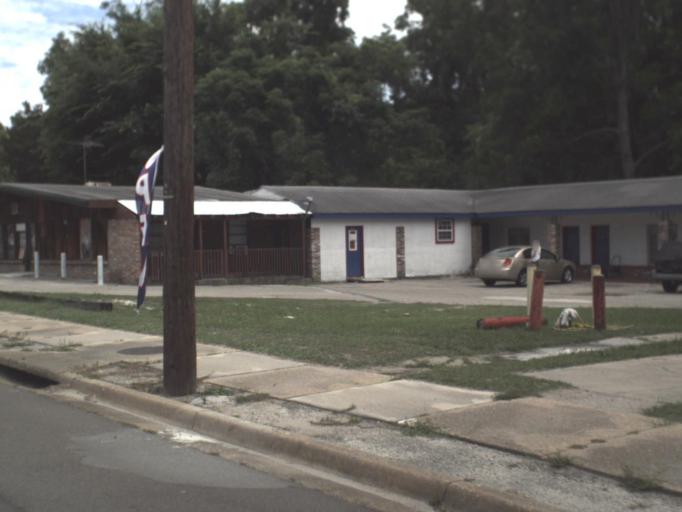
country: US
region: Florida
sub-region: Nassau County
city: Hilliard
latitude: 30.6891
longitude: -81.9164
